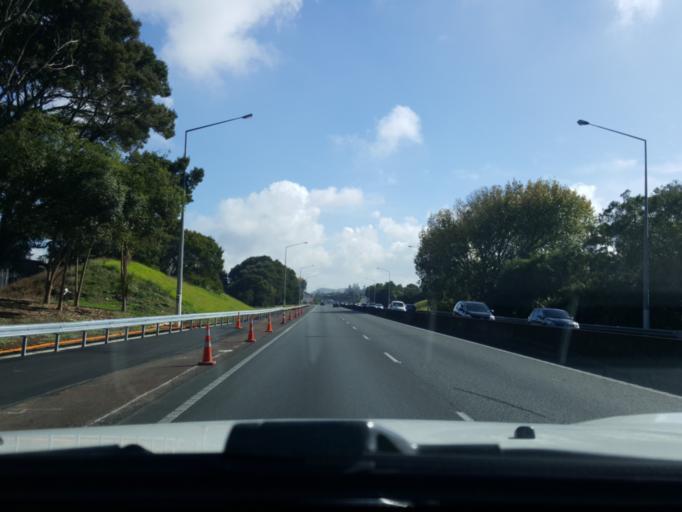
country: NZ
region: Auckland
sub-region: Auckland
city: Mangere
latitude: -36.9771
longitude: 174.8228
